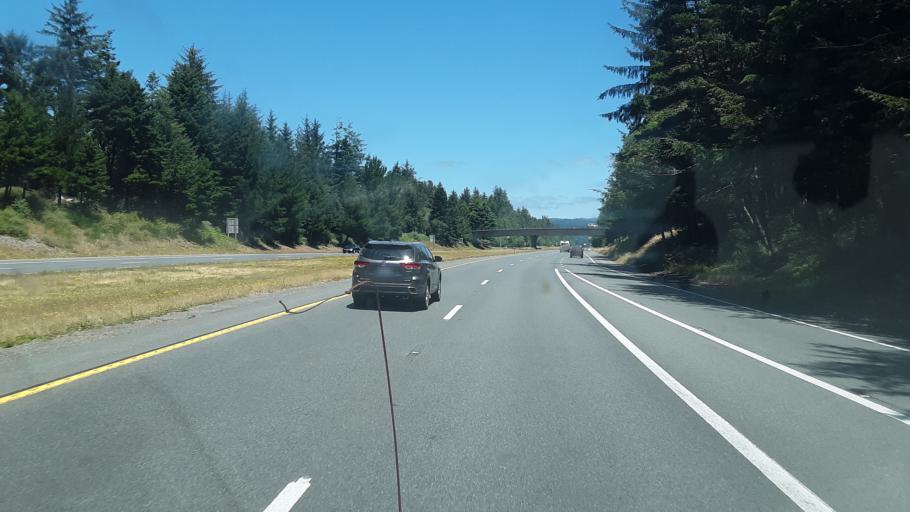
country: US
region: California
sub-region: Del Norte County
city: Crescent City
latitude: 41.7758
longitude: -124.1851
